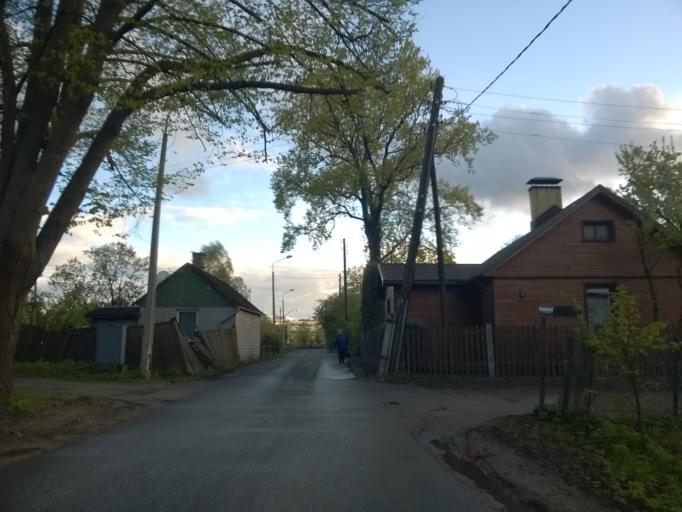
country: LV
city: Tireli
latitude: 56.9486
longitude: 23.6217
